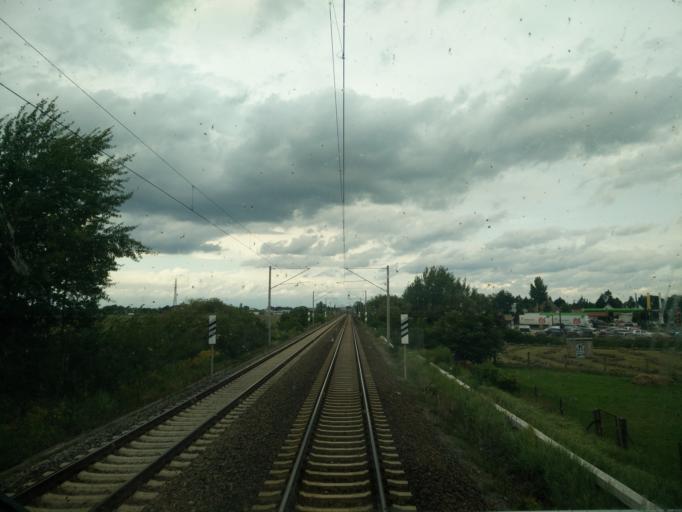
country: DE
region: Brandenburg
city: Luebben
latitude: 51.9206
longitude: 13.8948
